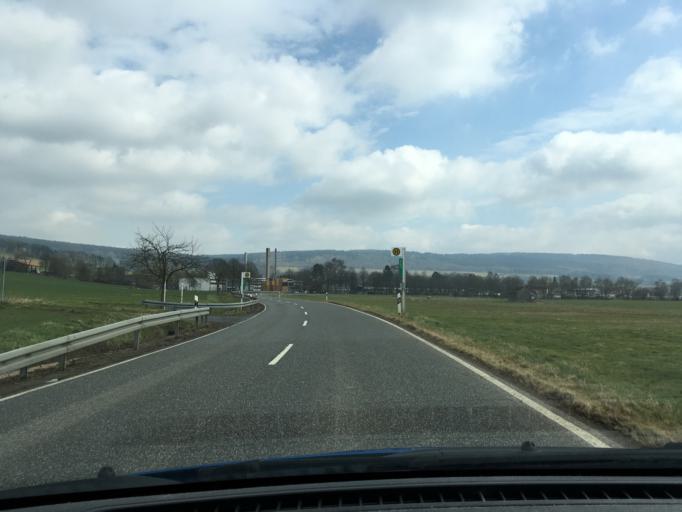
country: DE
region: Lower Saxony
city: Bodenfelde
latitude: 51.5970
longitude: 9.5850
